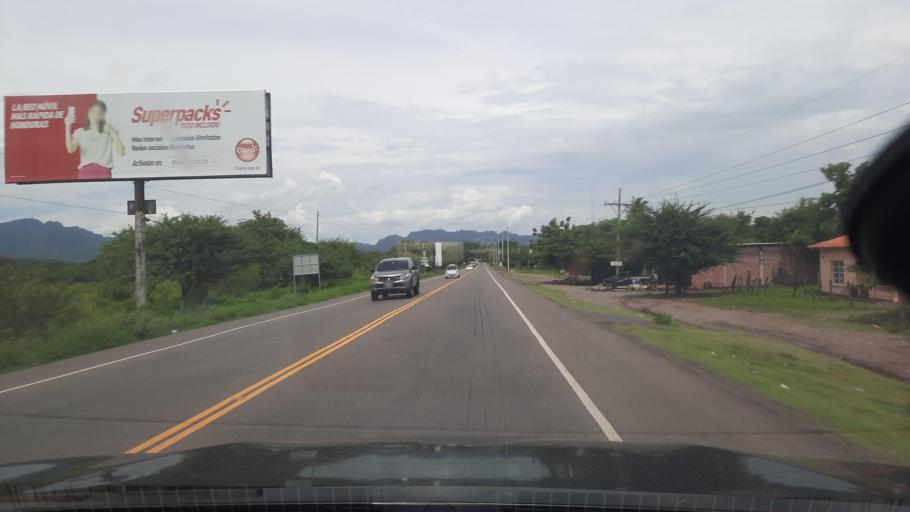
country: HN
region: Valle
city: Nacaome
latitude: 13.5396
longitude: -87.4692
